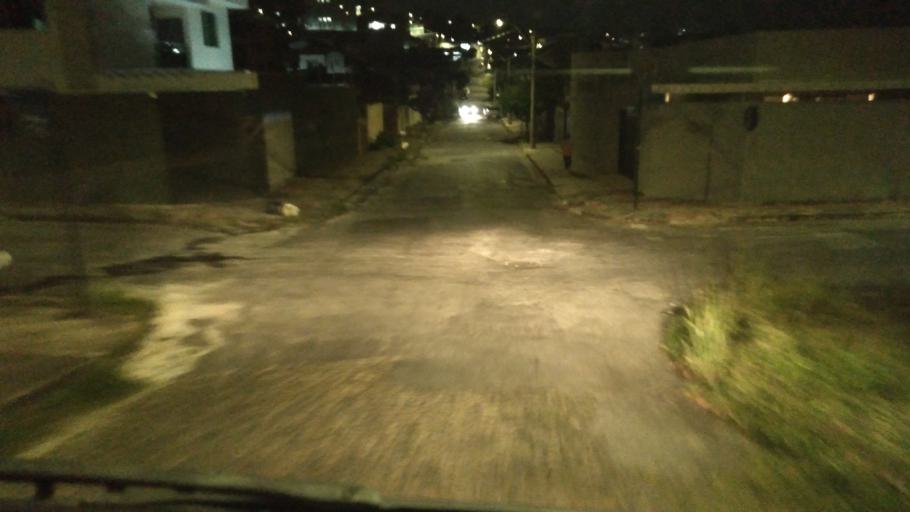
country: BR
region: Minas Gerais
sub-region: Belo Horizonte
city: Belo Horizonte
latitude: -19.8921
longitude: -43.9391
